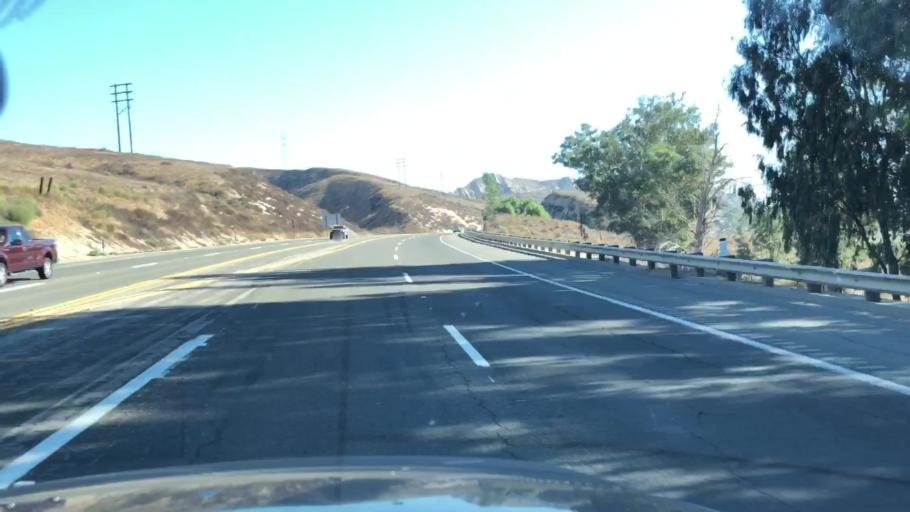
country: US
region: California
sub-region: Los Angeles County
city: Val Verde
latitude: 34.4205
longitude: -118.6560
